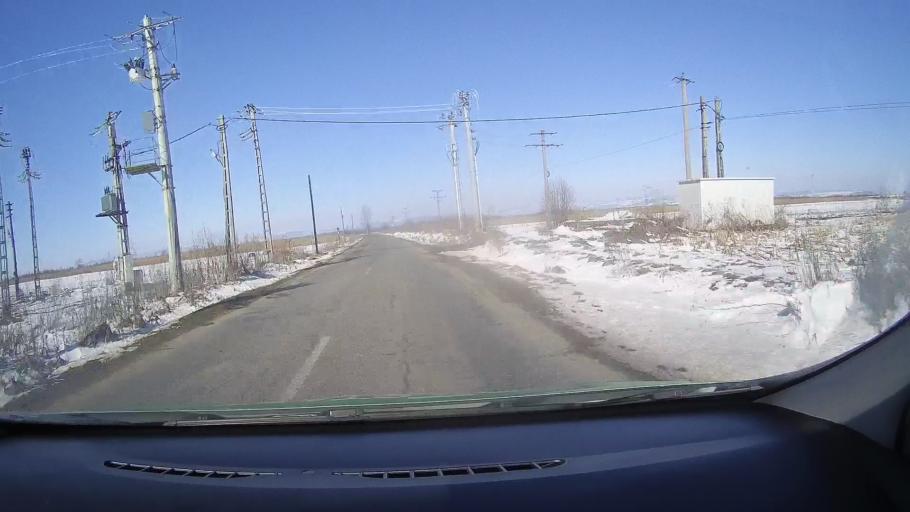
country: RO
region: Brasov
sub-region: Comuna Harseni
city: Harseni
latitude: 45.7633
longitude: 25.0065
